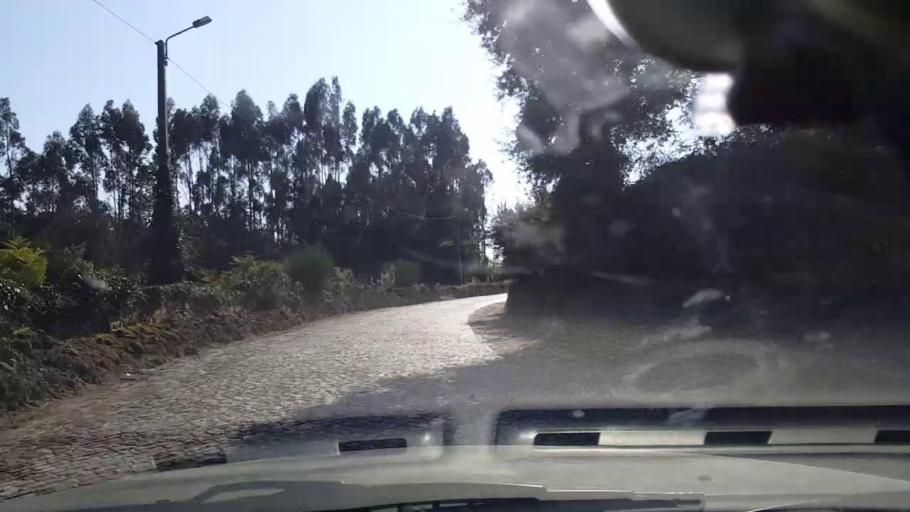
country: PT
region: Porto
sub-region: Vila do Conde
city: Arvore
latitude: 41.3550
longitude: -8.7026
